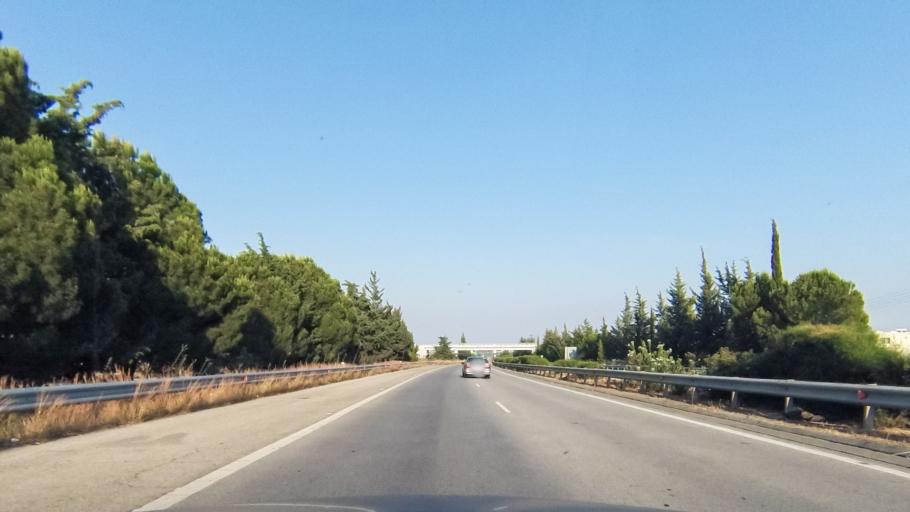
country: CY
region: Limassol
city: Ypsonas
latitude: 34.6965
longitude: 32.9632
